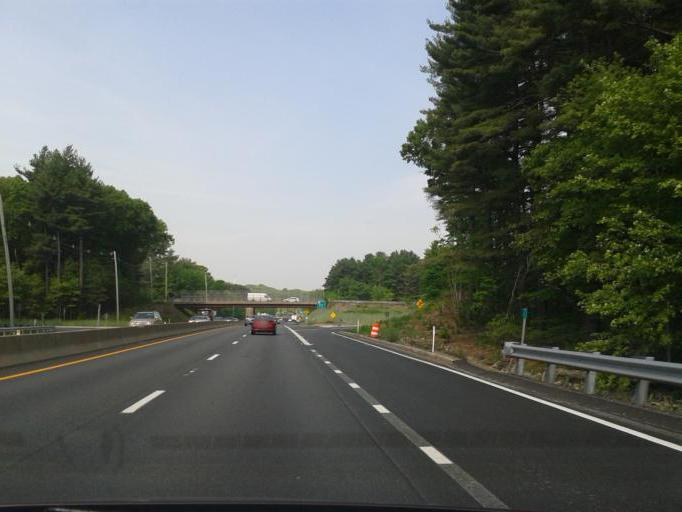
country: US
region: Massachusetts
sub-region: Worcester County
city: Southborough
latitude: 42.2922
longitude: -71.5244
